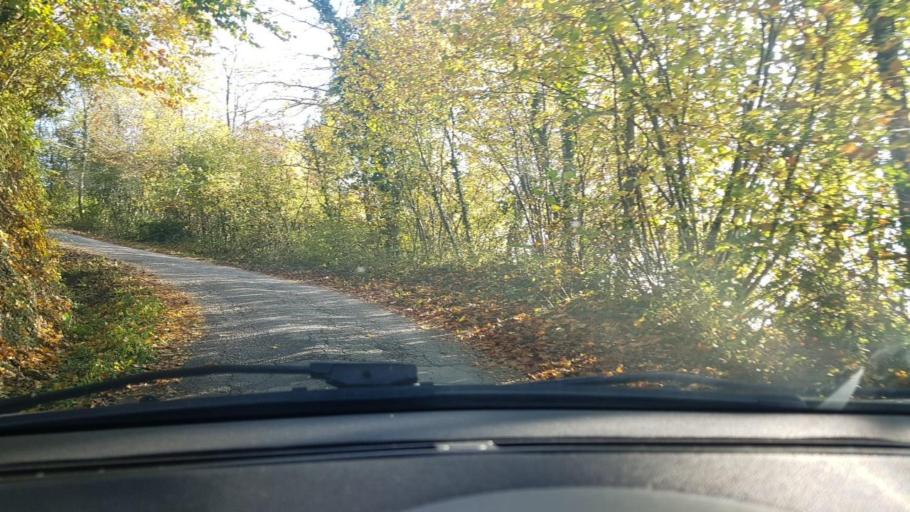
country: HR
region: Krapinsko-Zagorska
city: Zabok
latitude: 46.0350
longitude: 15.8858
